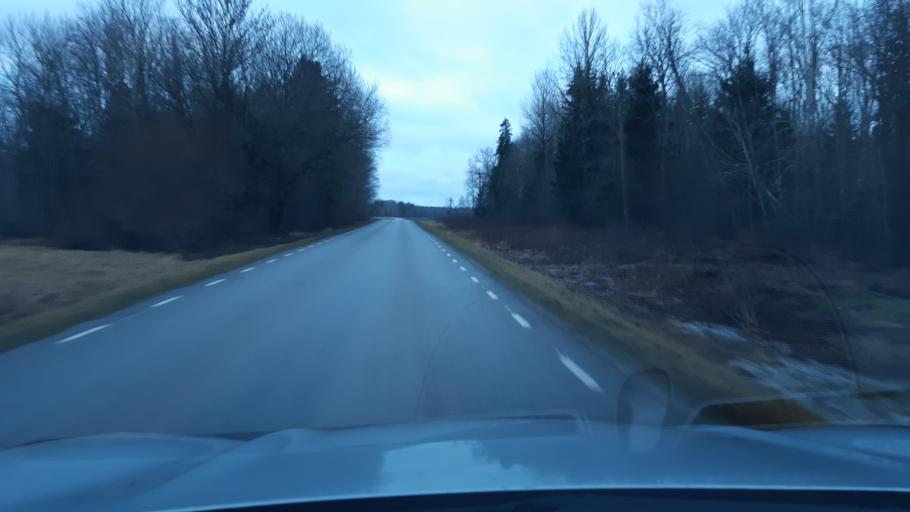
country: EE
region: Raplamaa
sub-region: Rapla vald
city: Rapla
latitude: 59.0390
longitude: 24.6772
